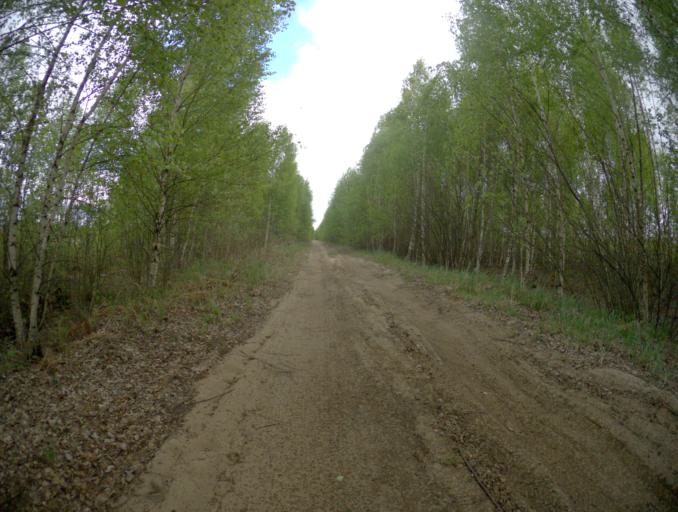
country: RU
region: Vladimir
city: Urshel'skiy
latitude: 55.5994
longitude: 40.1445
